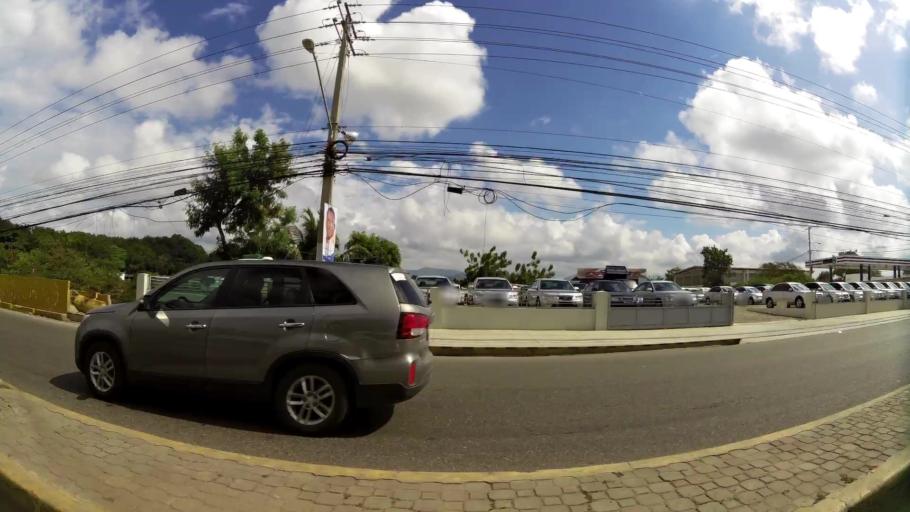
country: DO
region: Santiago
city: Santiago de los Caballeros
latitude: 19.4756
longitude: -70.6960
